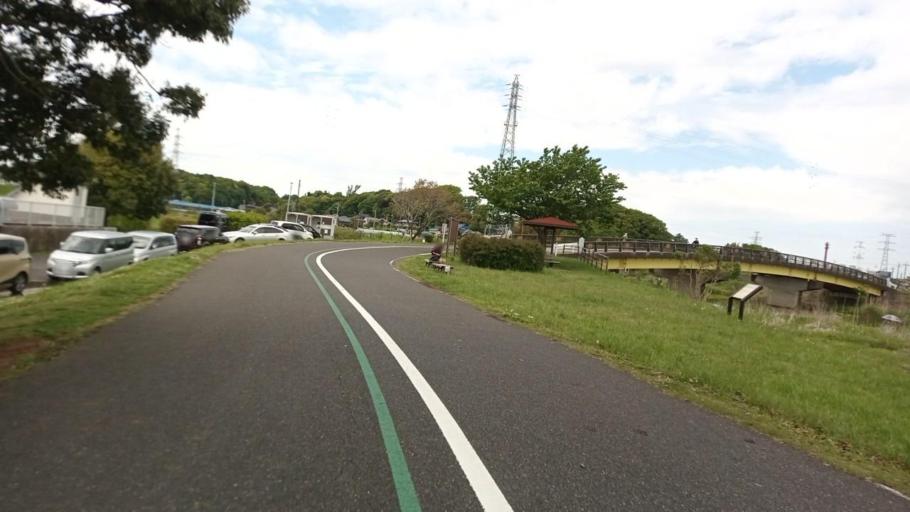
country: JP
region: Chiba
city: Abiko
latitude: 35.8584
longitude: 140.0033
